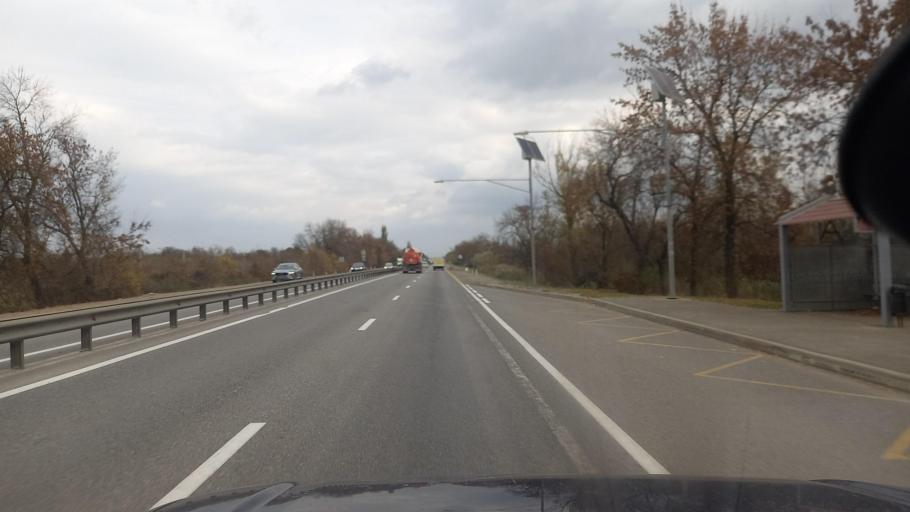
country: RU
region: Krasnodarskiy
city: Afipskiy
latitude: 44.8956
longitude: 38.8631
